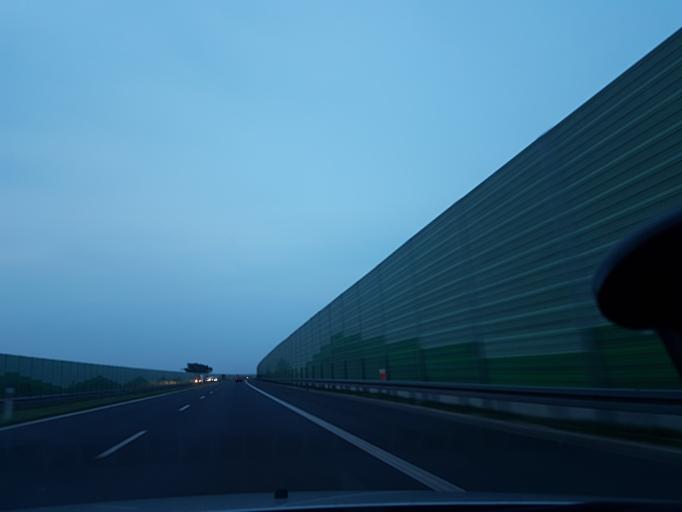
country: PL
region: Lodz Voivodeship
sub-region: Powiat leczycki
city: Piatek
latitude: 52.1204
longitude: 19.5003
